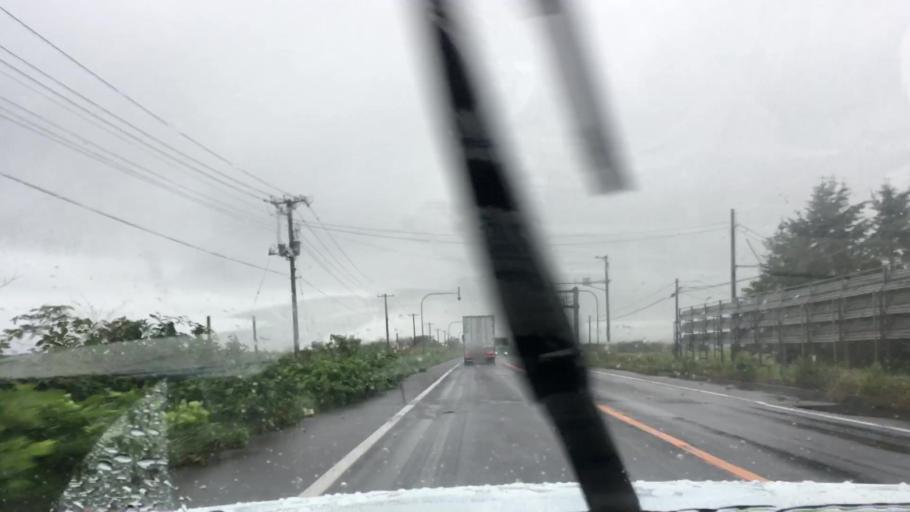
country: JP
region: Hokkaido
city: Niseko Town
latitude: 42.4310
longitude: 140.3181
